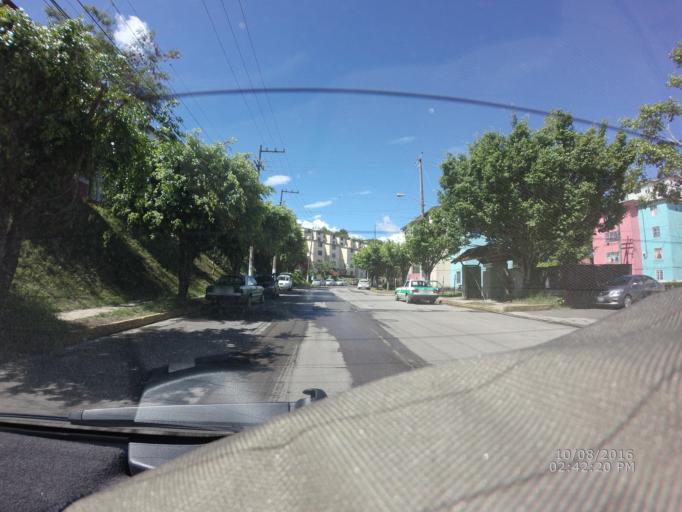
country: MX
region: Veracruz
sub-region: Xalapa
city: Lomas Verdes
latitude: 19.5103
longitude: -96.9016
